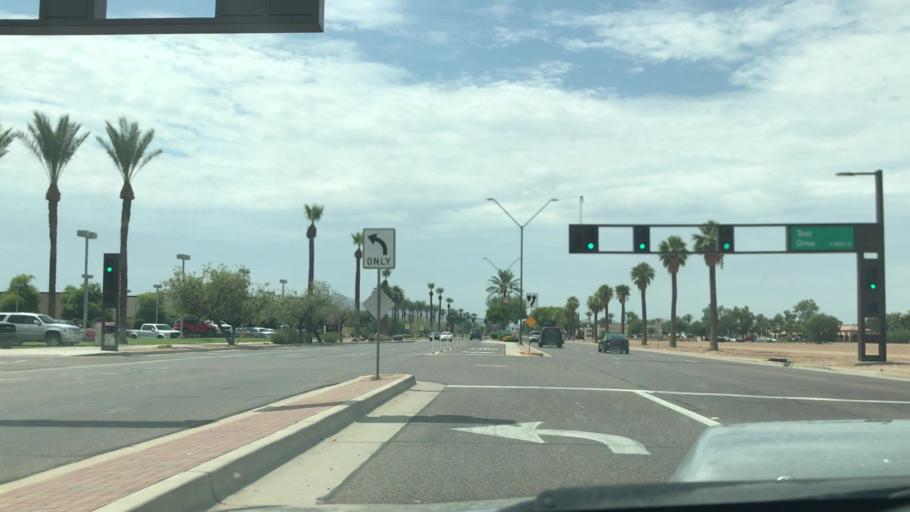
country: US
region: Arizona
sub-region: Maricopa County
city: Goodyear
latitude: 33.4555
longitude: -112.3582
